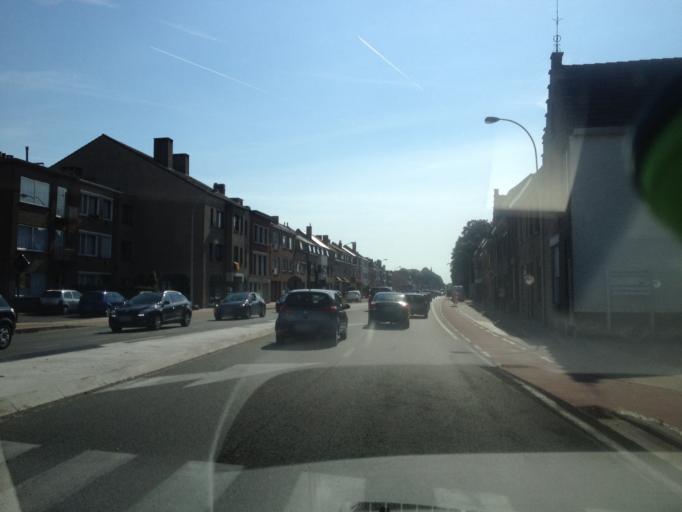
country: BE
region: Flanders
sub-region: Provincie West-Vlaanderen
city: Brugge
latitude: 51.2001
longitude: 3.1944
